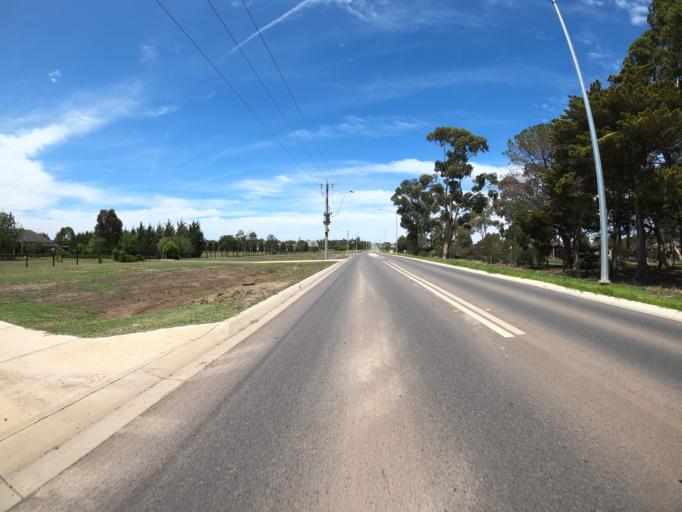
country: AU
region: Victoria
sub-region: Hume
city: Craigieburn
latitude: -37.5666
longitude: 144.9154
